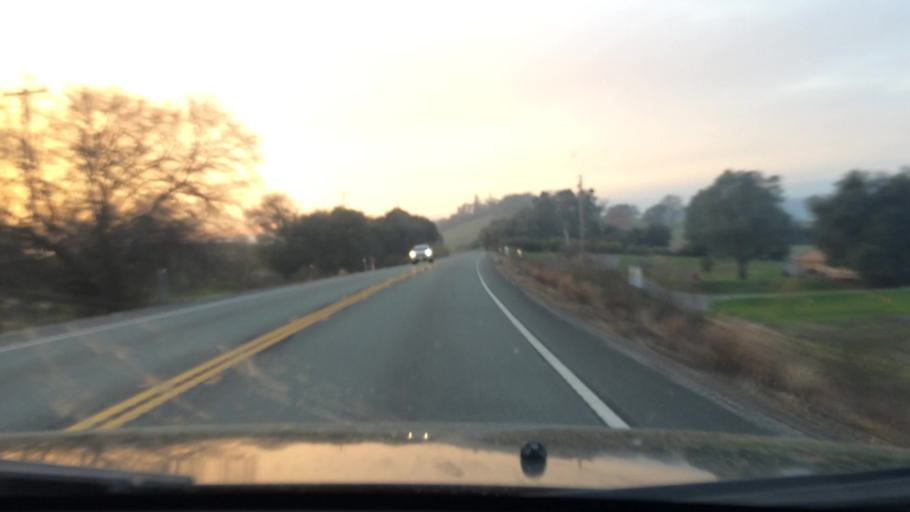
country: US
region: California
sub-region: Amador County
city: Jackson
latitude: 38.2975
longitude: -120.7209
